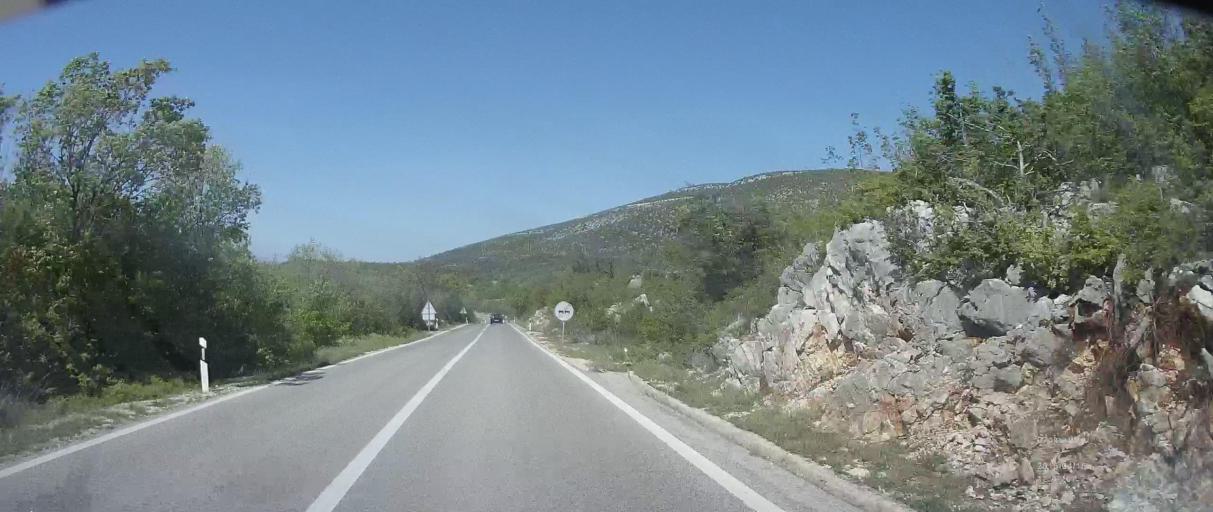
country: HR
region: Sibensko-Kniniska
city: Rogoznica
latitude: 43.6268
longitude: 16.0932
